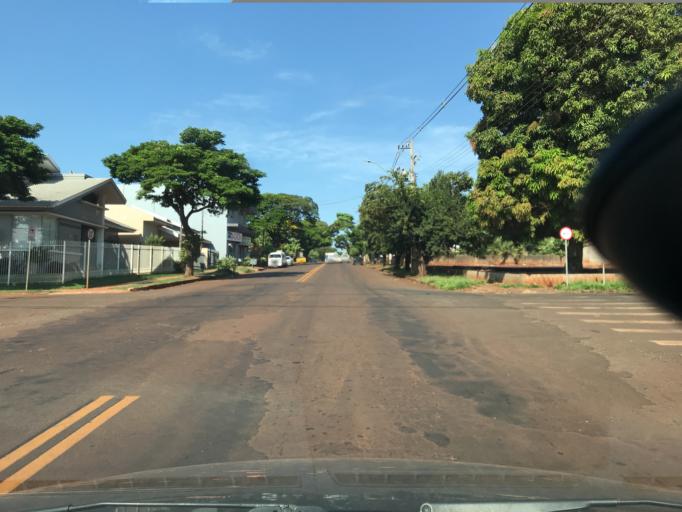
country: BR
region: Parana
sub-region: Palotina
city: Palotina
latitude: -24.2888
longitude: -53.8355
